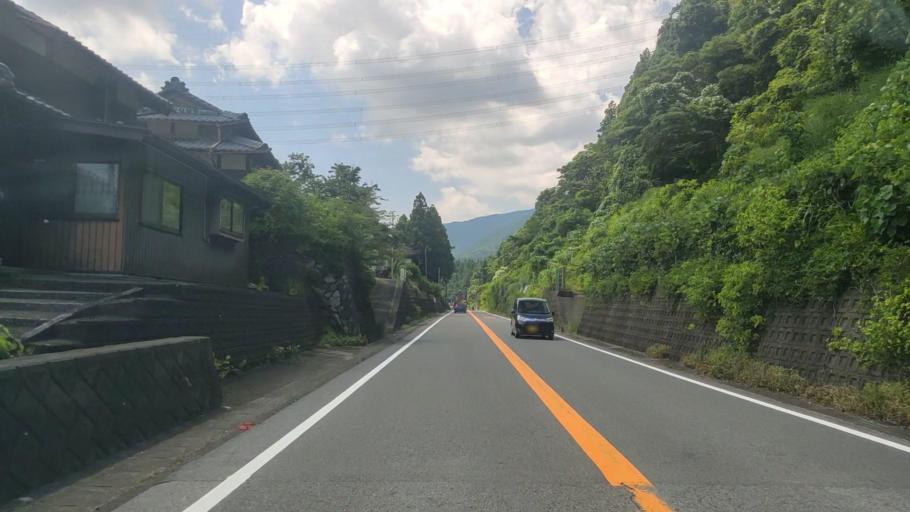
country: JP
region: Gifu
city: Tarui
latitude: 35.3779
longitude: 136.4406
